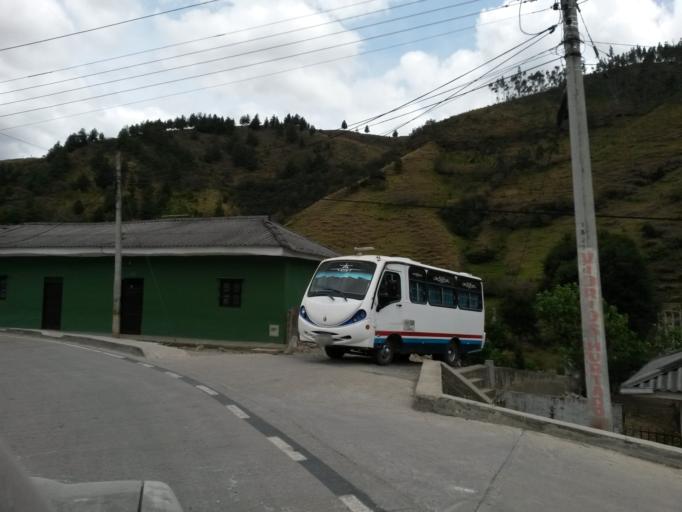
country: CO
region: Cauca
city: Totoro
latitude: 2.5121
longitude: -76.4004
